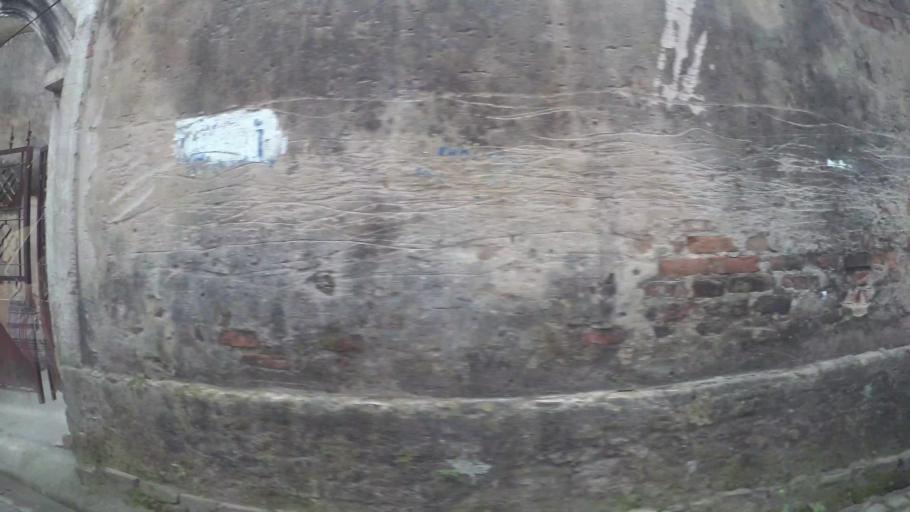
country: VN
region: Ha Noi
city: Trau Quy
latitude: 21.0717
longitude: 105.9185
